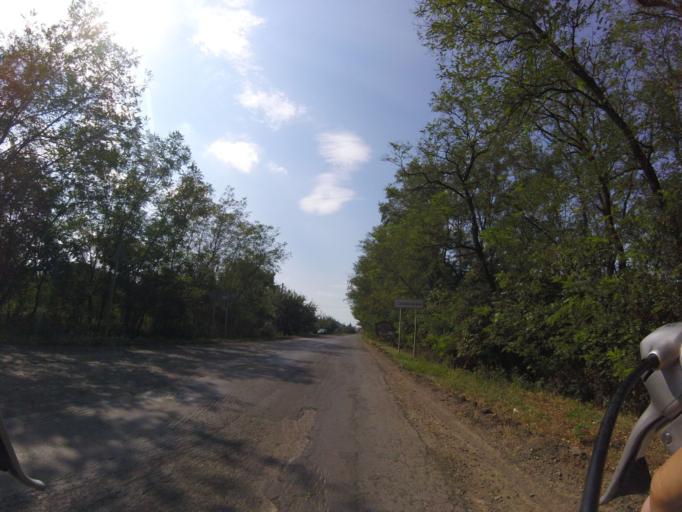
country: HU
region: Szabolcs-Szatmar-Bereg
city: Gyulahaza
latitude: 48.1521
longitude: 22.1492
